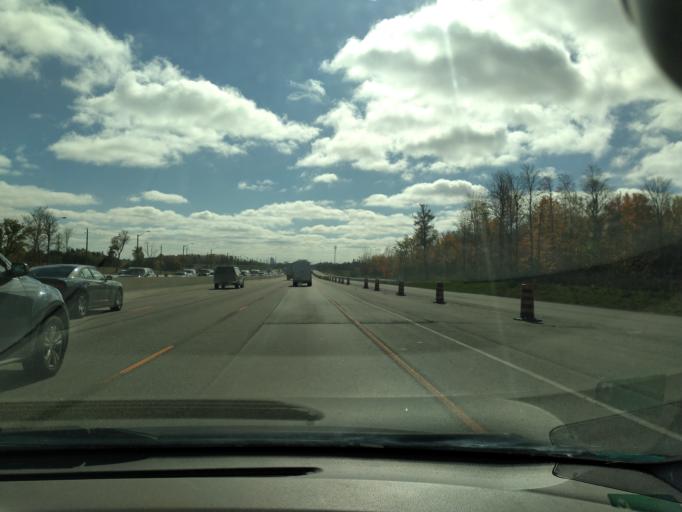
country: CA
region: Ontario
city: Vaughan
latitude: 43.8921
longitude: -79.5595
